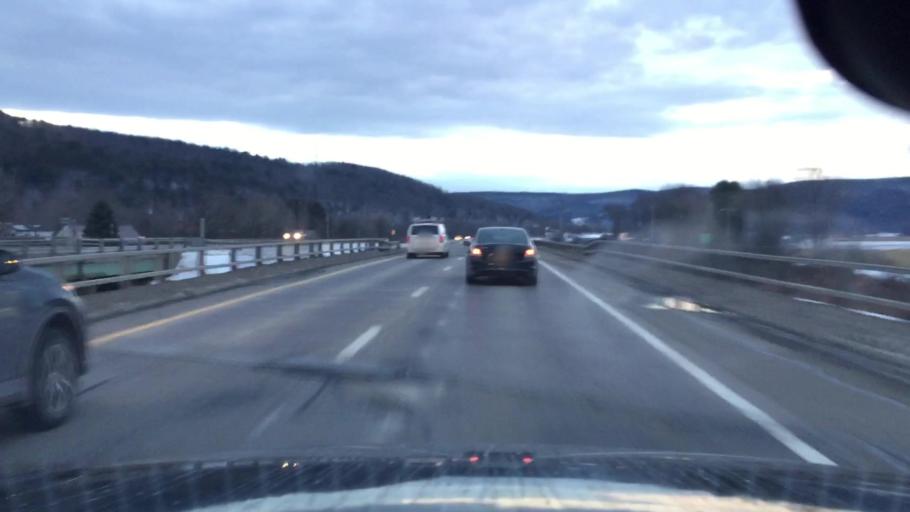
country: US
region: New York
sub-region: Steuben County
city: Gang Mills
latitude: 42.2074
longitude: -77.1702
